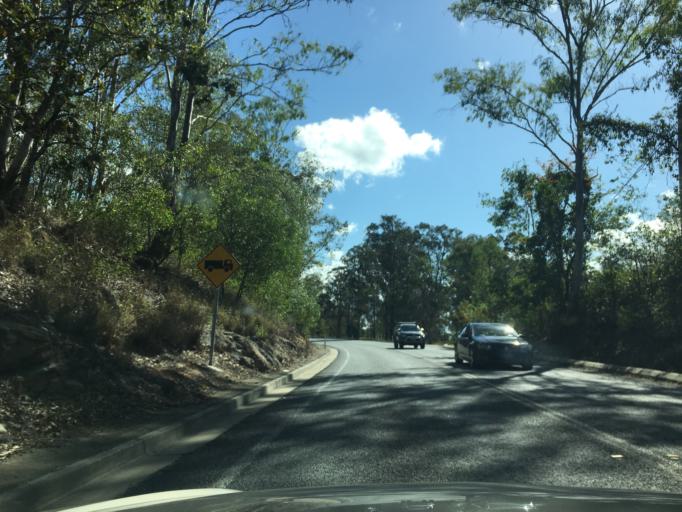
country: AU
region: Queensland
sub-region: Logan
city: Chambers Flat
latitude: -27.7571
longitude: 153.1139
